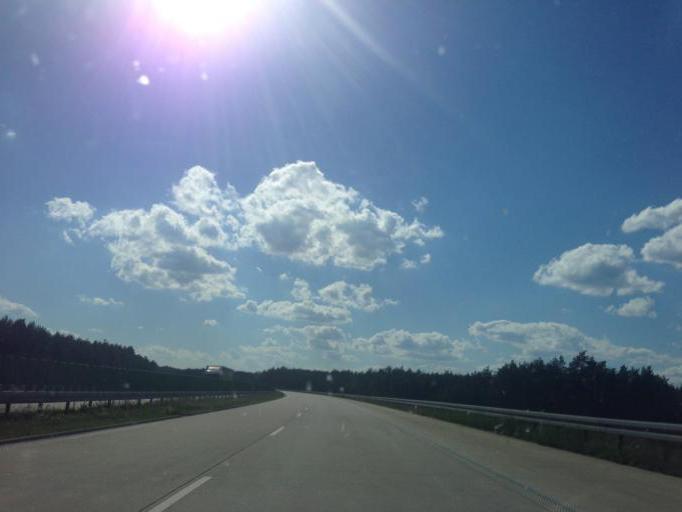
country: PL
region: Lower Silesian Voivodeship
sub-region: Powiat boleslawiecki
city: Boleslawiec
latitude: 51.3116
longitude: 15.5482
